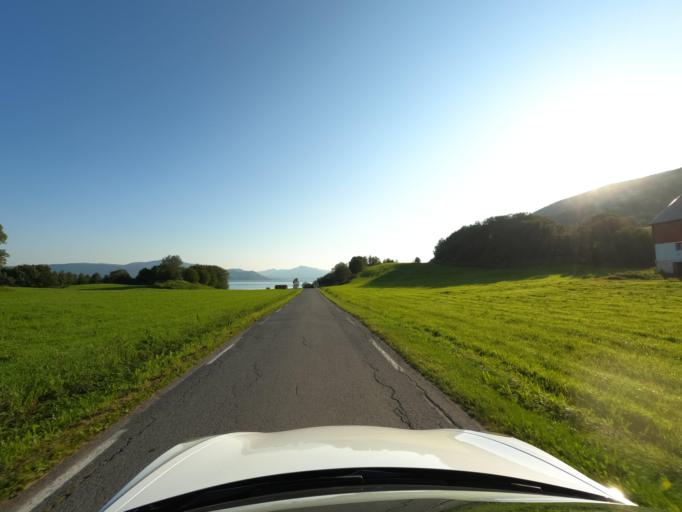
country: NO
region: Nordland
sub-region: Ballangen
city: Ballangen
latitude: 68.4710
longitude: 16.8689
